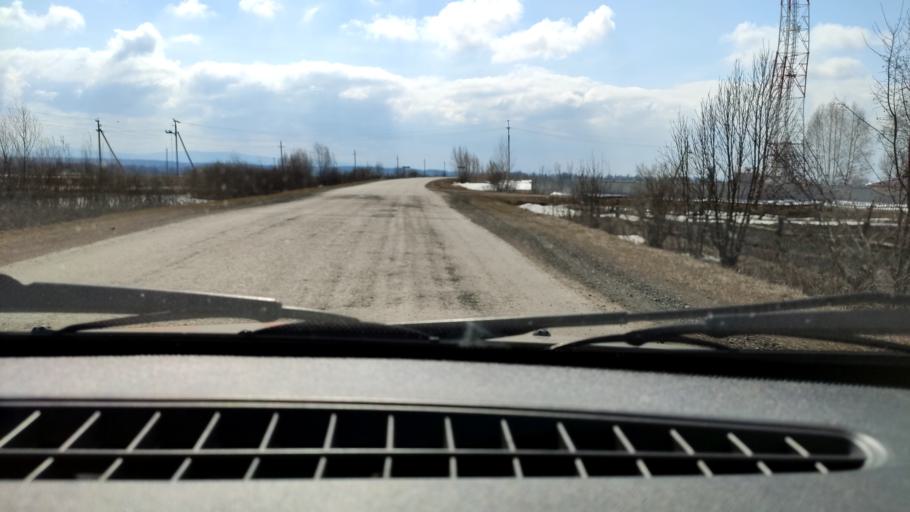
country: RU
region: Bashkortostan
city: Kudeyevskiy
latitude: 54.8448
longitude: 56.7956
